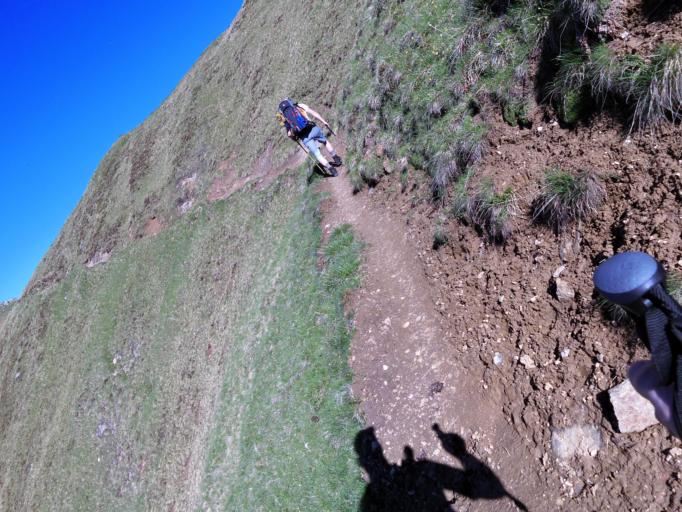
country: AT
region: Tyrol
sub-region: Politischer Bezirk Innsbruck Land
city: Neustift im Stubaital
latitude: 47.1310
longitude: 11.2759
